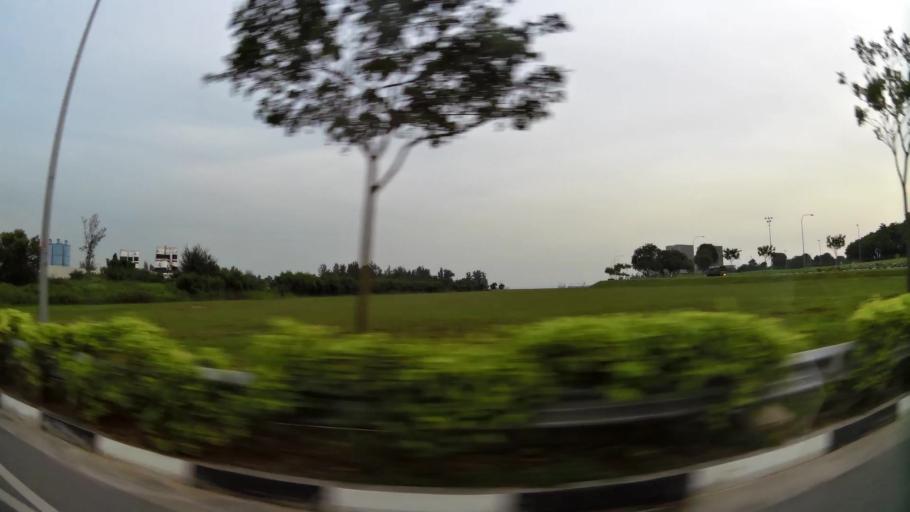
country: SG
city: Singapore
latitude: 1.2880
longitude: 103.8774
